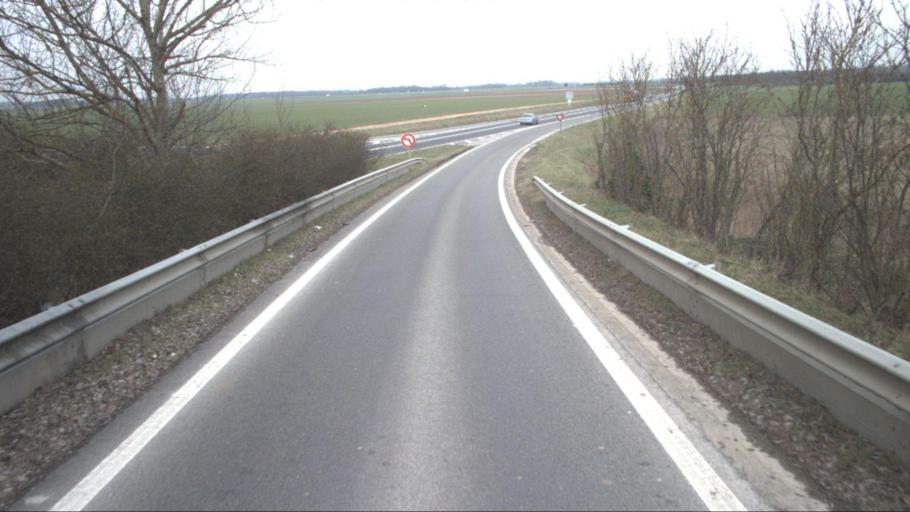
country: FR
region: Ile-de-France
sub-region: Departement des Yvelines
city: Ablis
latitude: 48.5101
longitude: 1.8320
